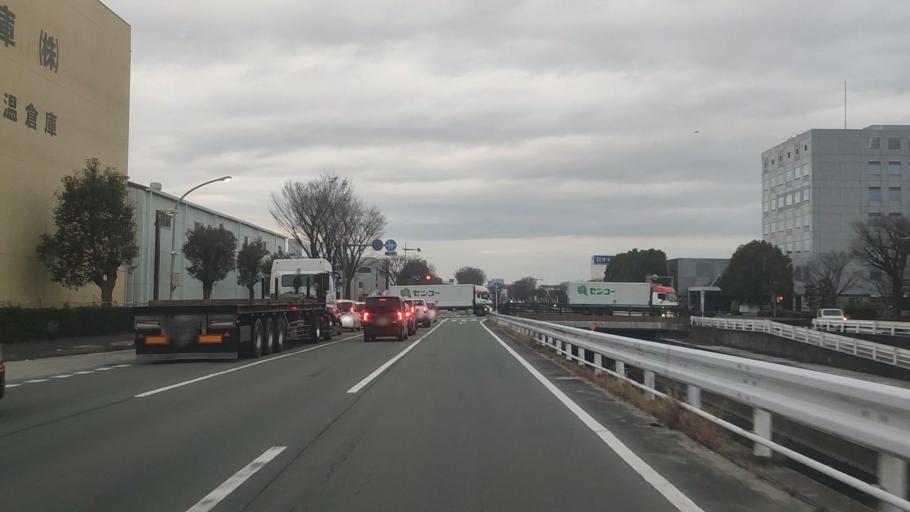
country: JP
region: Kumamoto
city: Kumamoto
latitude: 32.7659
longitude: 130.7050
